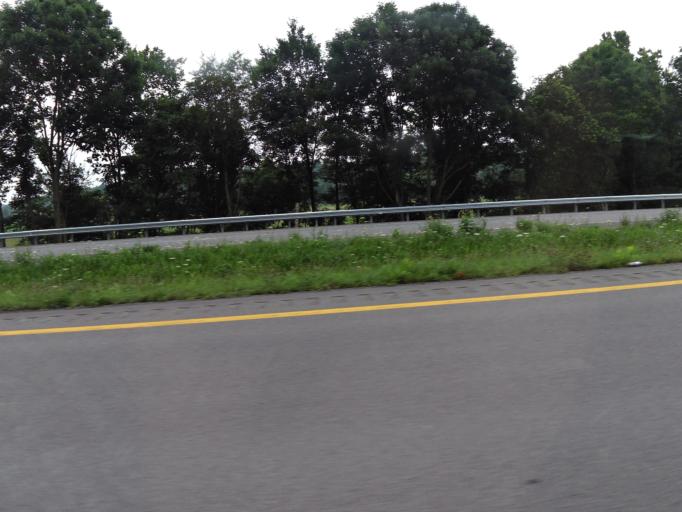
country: US
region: Kentucky
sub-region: Grayson County
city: Leitchfield
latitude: 37.4097
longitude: -86.4489
